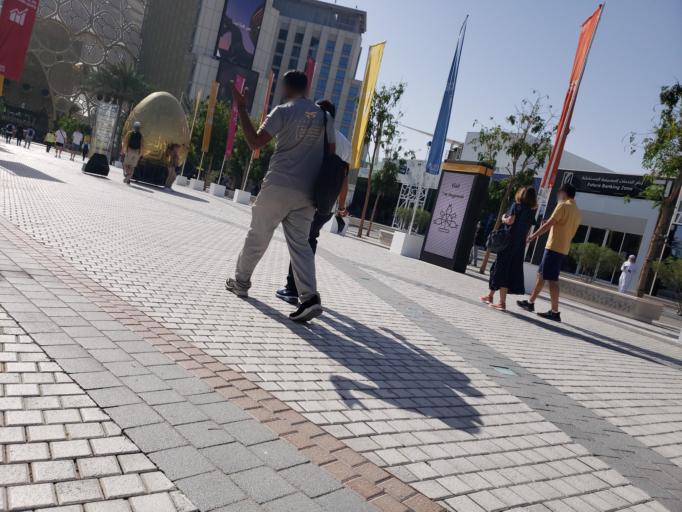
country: AE
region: Dubai
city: Dubai
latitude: 24.9619
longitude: 55.1489
